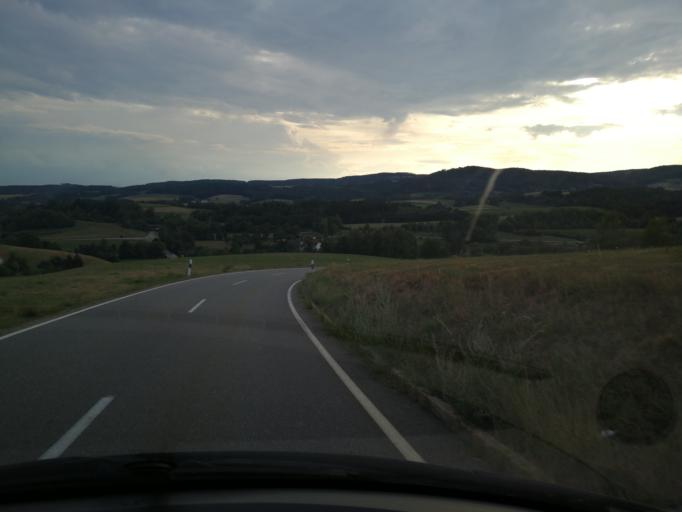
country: DE
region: Bavaria
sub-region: Lower Bavaria
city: Rattiszell
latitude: 49.0357
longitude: 12.6645
